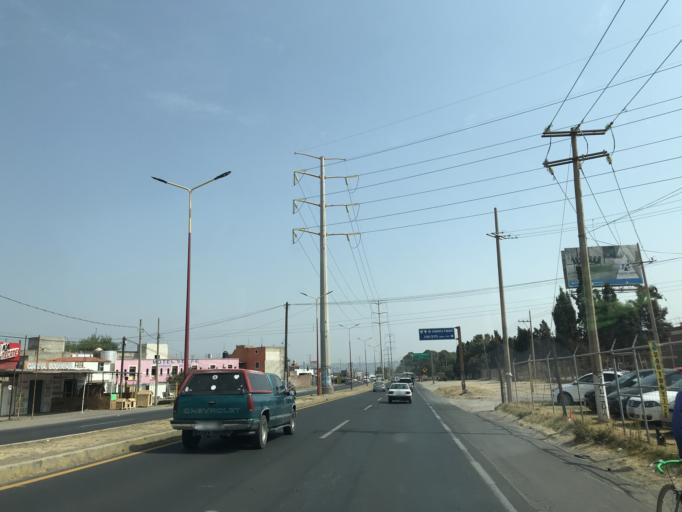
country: MX
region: Tlaxcala
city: La Magdalena Tlaltelulco
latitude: 19.2934
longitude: -98.1951
